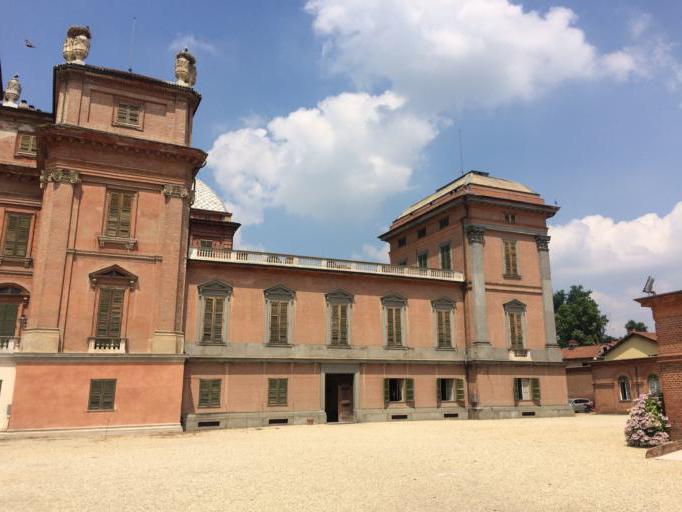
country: IT
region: Piedmont
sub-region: Provincia di Cuneo
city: Racconigi
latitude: 44.7687
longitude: 7.6759
